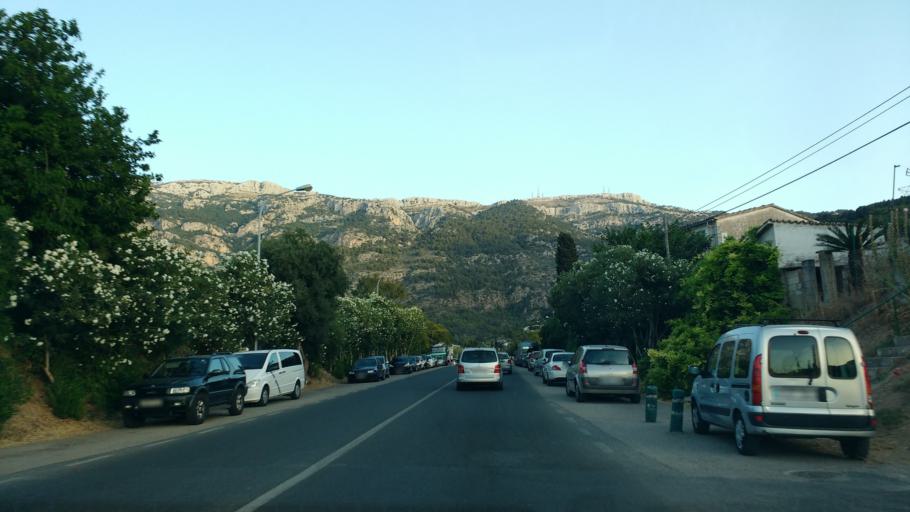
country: ES
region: Balearic Islands
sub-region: Illes Balears
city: Soller
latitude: 39.7708
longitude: 2.7063
